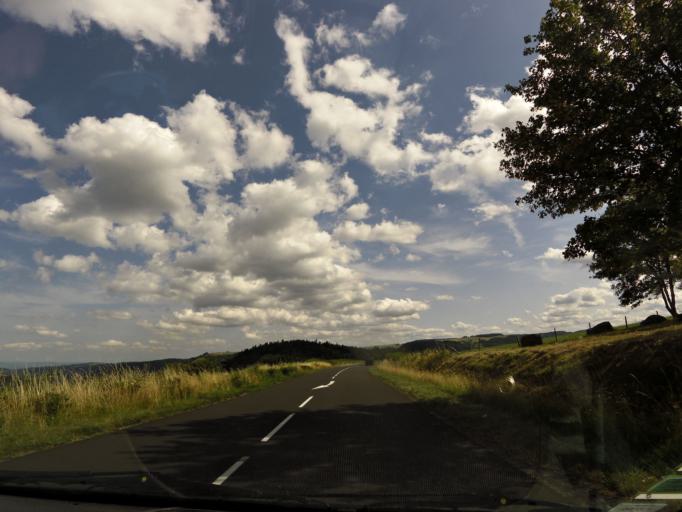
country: FR
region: Auvergne
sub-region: Departement du Puy-de-Dome
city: Aydat
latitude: 45.5378
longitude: 2.9477
